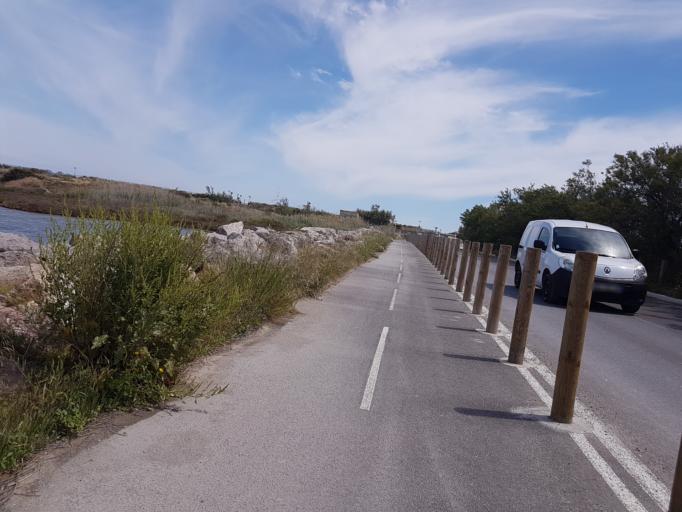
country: FR
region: Languedoc-Roussillon
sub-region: Departement de l'Herault
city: Vic-la-Gardiole
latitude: 43.4551
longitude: 3.8112
